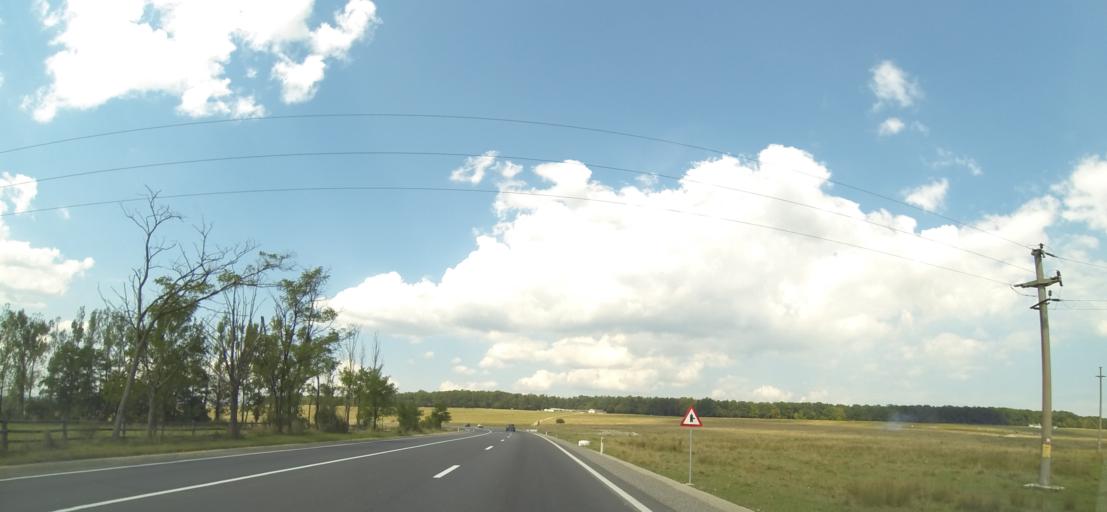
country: RO
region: Brasov
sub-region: Comuna Dumbravita
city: Dumbravita
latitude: 45.7457
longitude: 25.4138
